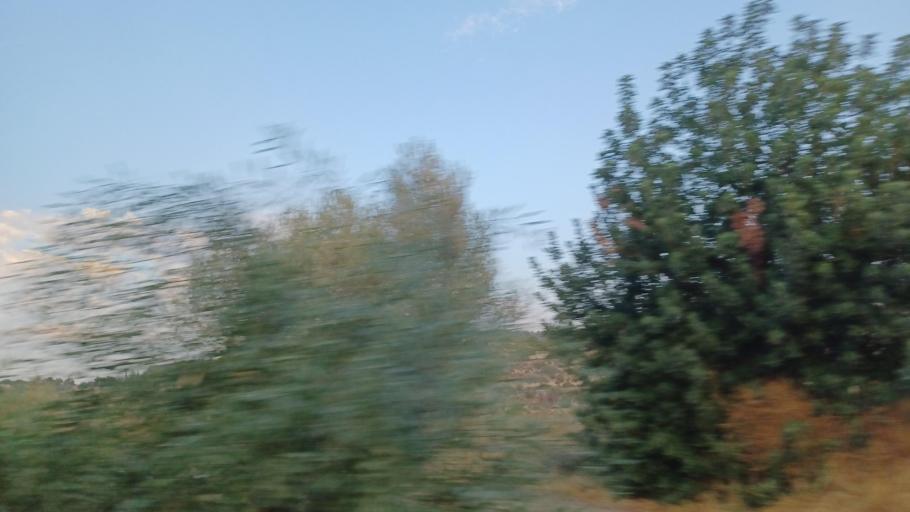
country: CY
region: Limassol
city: Pano Polemidia
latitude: 34.7511
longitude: 32.9735
